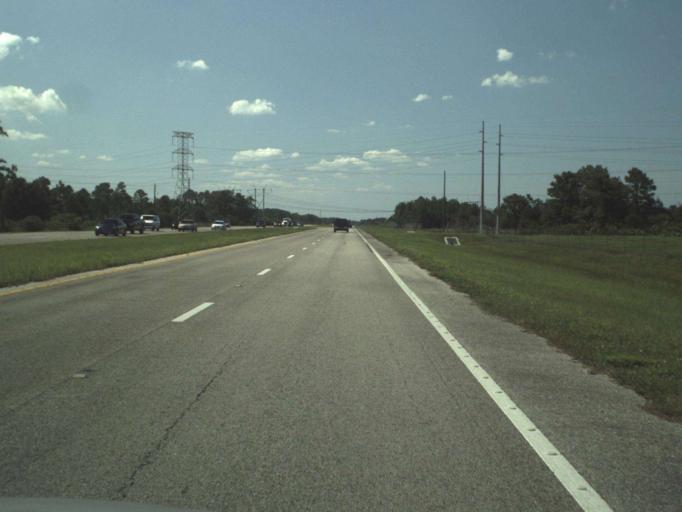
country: US
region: Florida
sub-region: Orange County
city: Wedgefield
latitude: 28.5014
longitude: -81.0506
